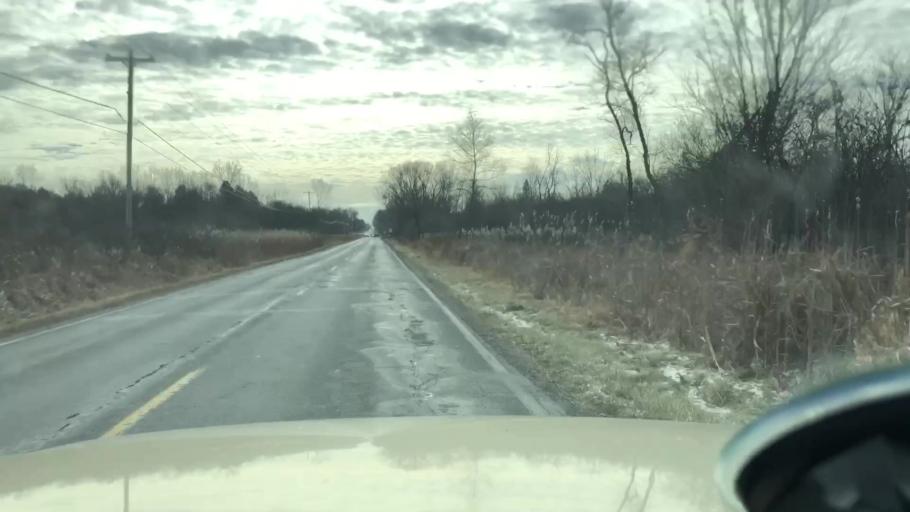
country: US
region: Michigan
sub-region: Jackson County
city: Jackson
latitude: 42.2679
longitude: -84.3649
